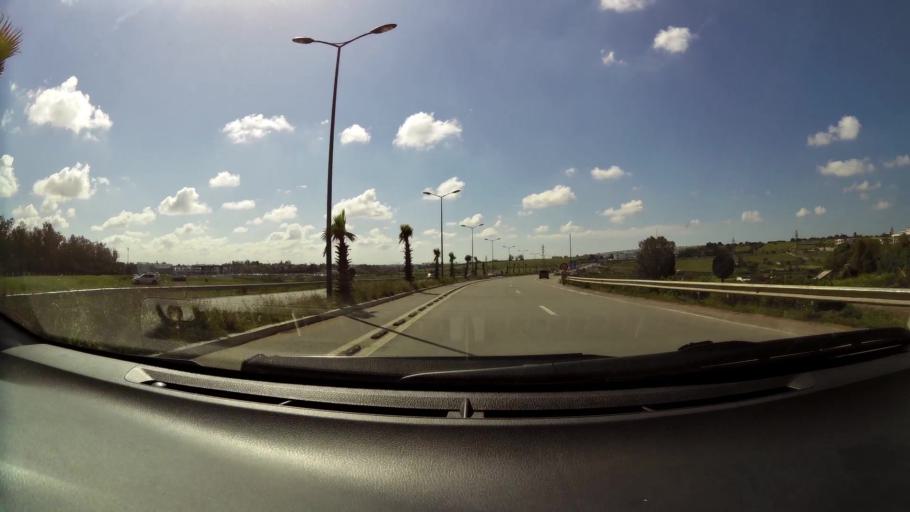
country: MA
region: Grand Casablanca
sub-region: Nouaceur
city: Bouskoura
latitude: 33.4825
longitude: -7.6300
